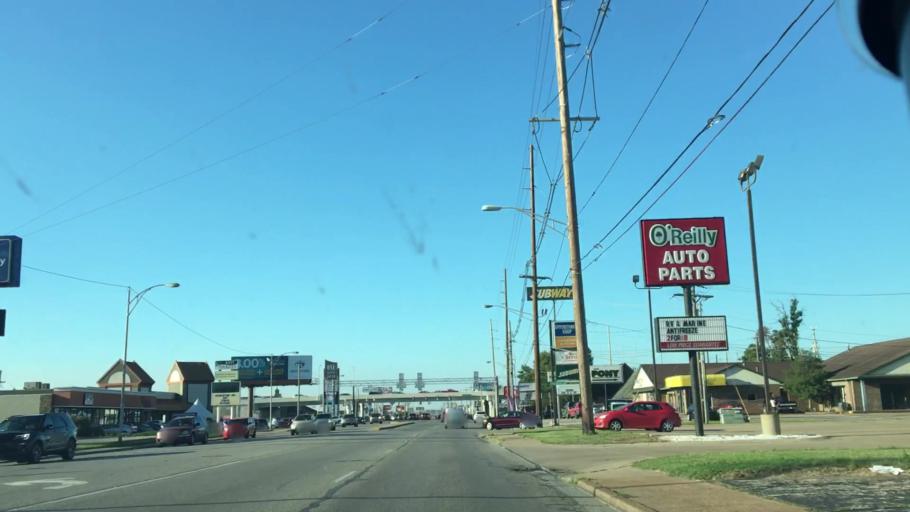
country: US
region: Indiana
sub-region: Vanderburgh County
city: Melody Hill
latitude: 37.9741
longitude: -87.4925
